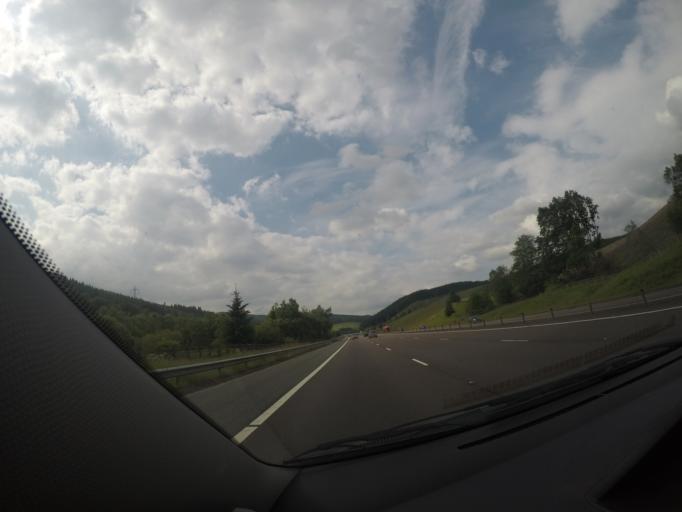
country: GB
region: Scotland
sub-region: Dumfries and Galloway
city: Moffat
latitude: 55.3527
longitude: -3.5081
